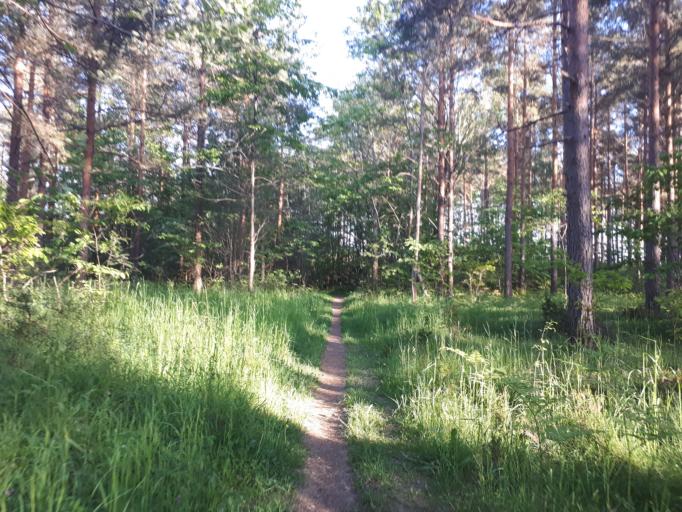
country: SE
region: Gotland
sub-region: Gotland
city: Visby
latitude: 57.6033
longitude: 18.2993
